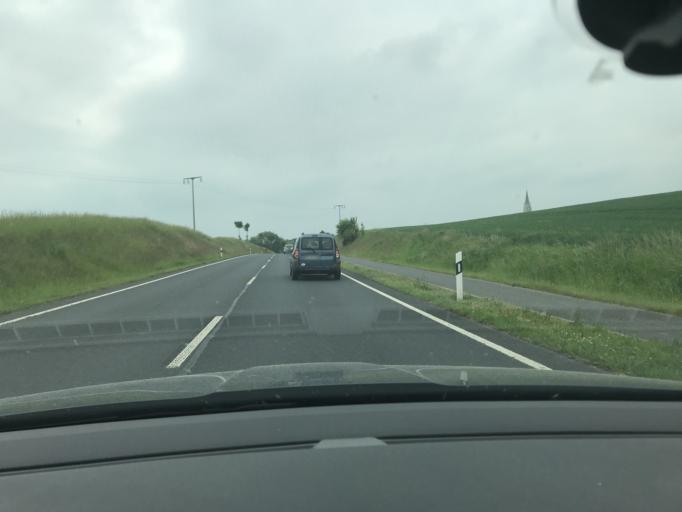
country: DE
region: Saxony
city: Priestewitz
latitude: 51.2427
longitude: 13.5033
